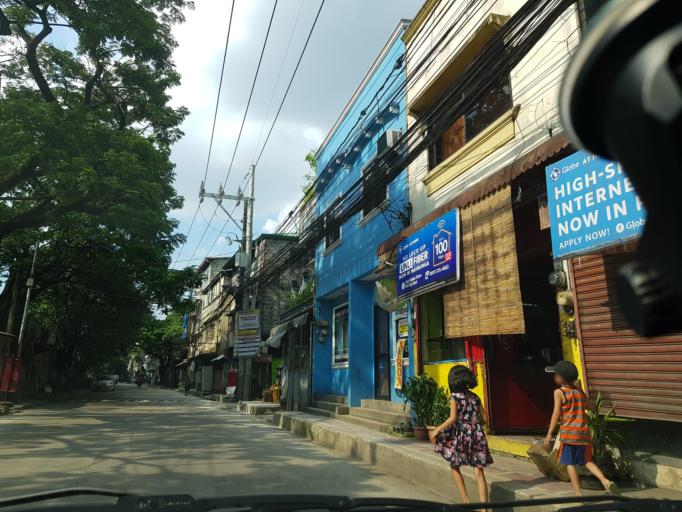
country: PH
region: Calabarzon
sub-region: Province of Rizal
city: Cainta
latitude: 14.5774
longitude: 121.0938
